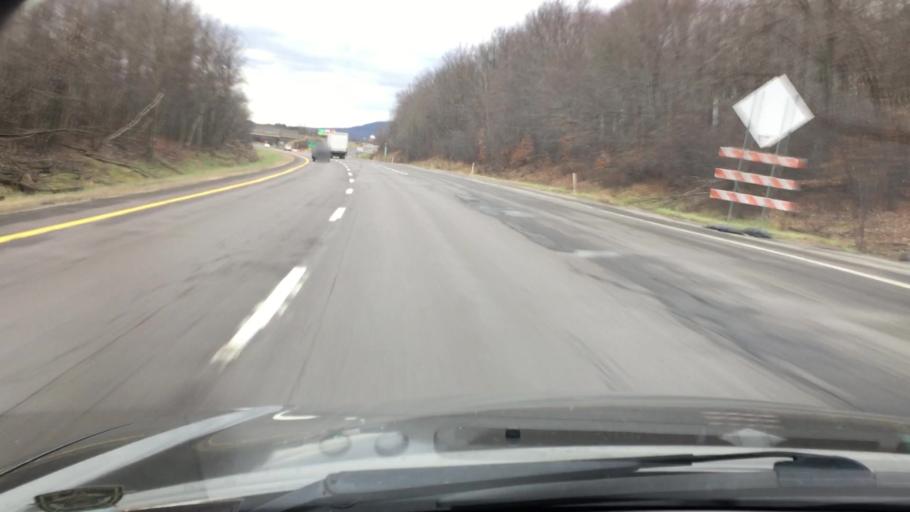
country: US
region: Pennsylvania
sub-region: Luzerne County
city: White Haven
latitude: 41.0608
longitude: -75.7434
